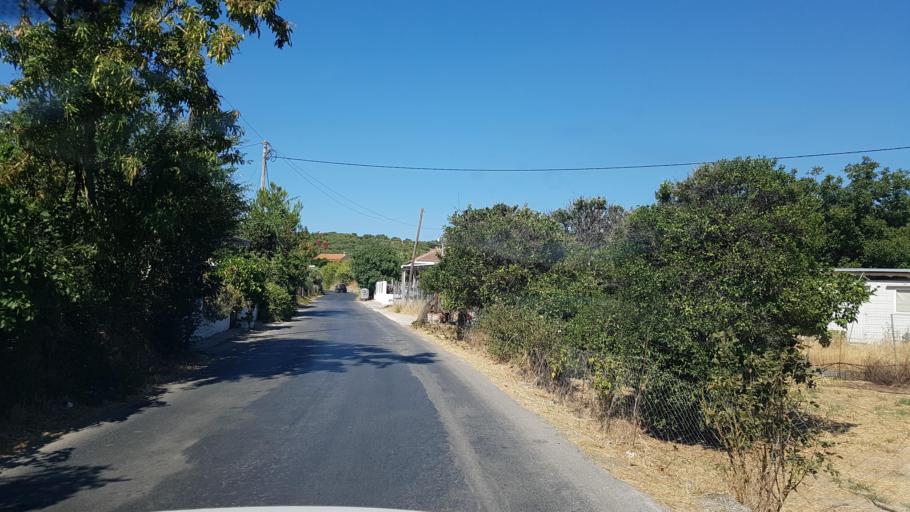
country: GR
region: Crete
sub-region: Nomos Chanias
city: Kissamos
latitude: 35.4865
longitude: 23.6897
